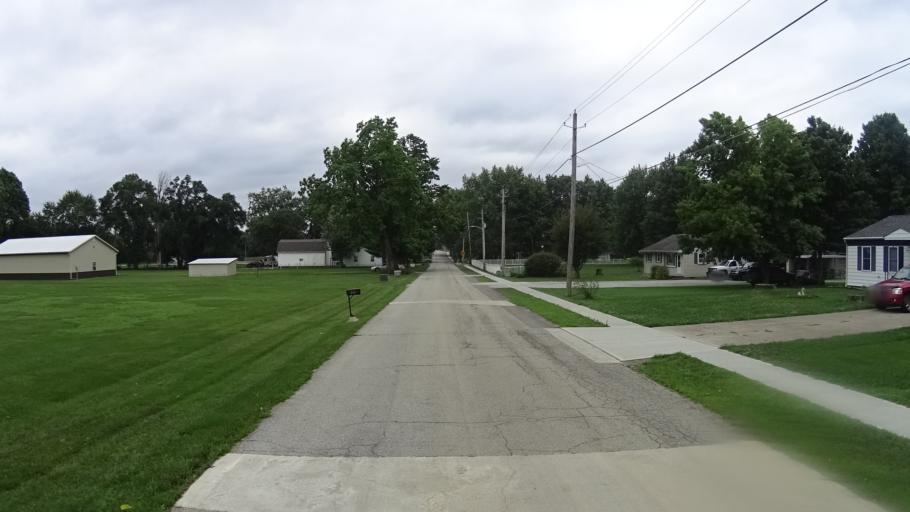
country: US
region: Indiana
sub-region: Madison County
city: Pendleton
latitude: 39.9912
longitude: -85.7443
